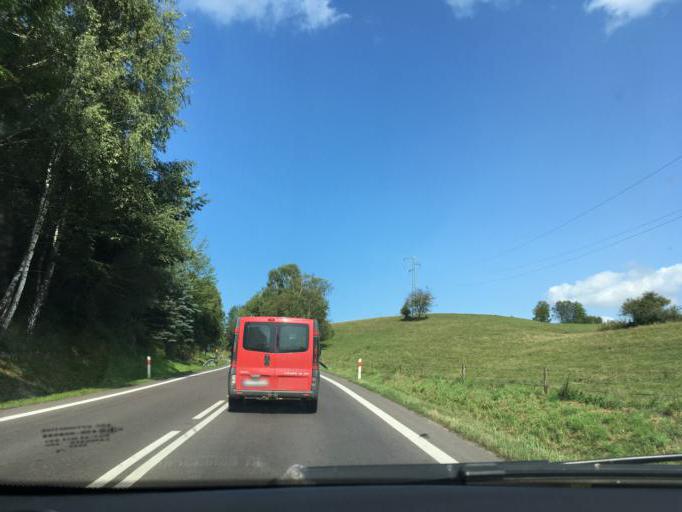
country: PL
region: Subcarpathian Voivodeship
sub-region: Powiat leski
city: Lesko
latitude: 49.4972
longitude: 22.3064
